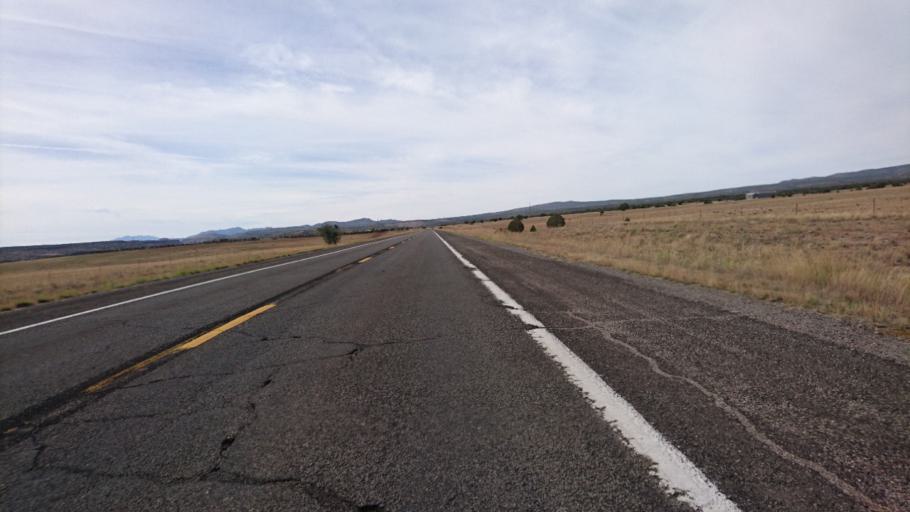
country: US
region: Arizona
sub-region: Mohave County
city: Peach Springs
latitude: 35.4663
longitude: -113.6017
